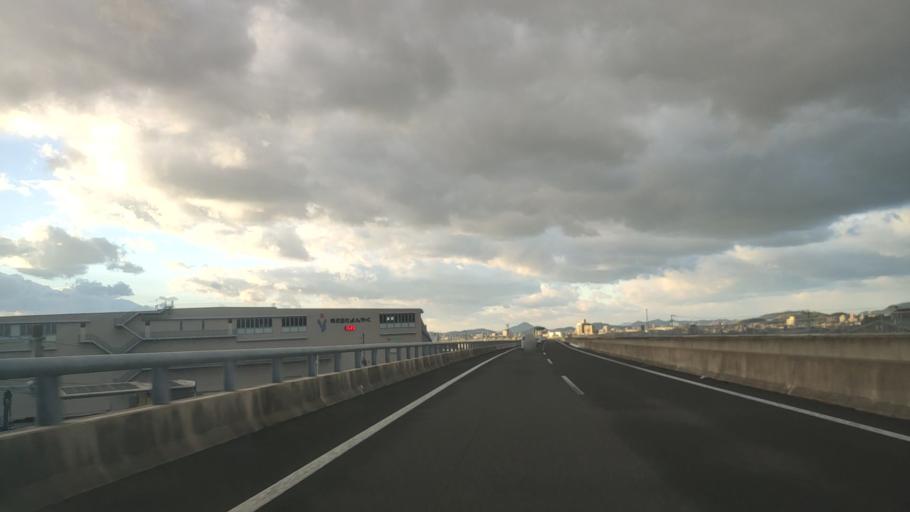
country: JP
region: Ehime
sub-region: Shikoku-chuo Shi
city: Matsuyama
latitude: 33.7898
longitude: 132.8055
